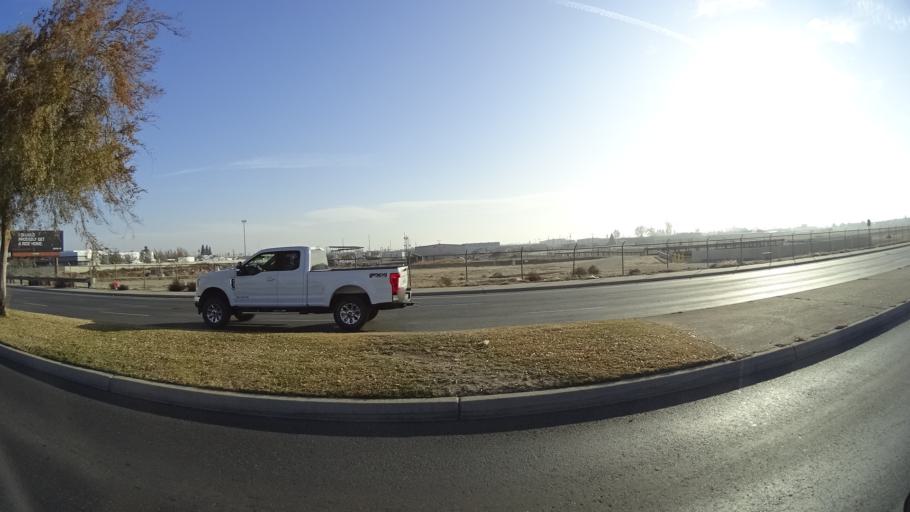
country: US
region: California
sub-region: Kern County
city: Greenacres
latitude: 35.3880
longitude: -119.0924
